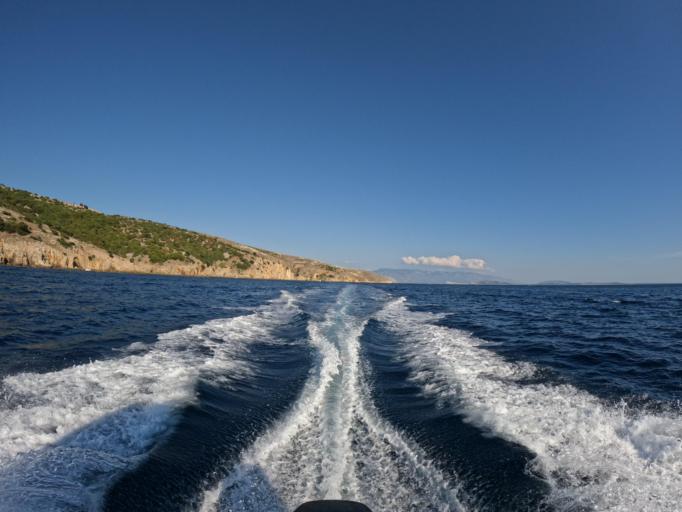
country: HR
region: Primorsko-Goranska
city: Punat
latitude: 44.9748
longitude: 14.6247
